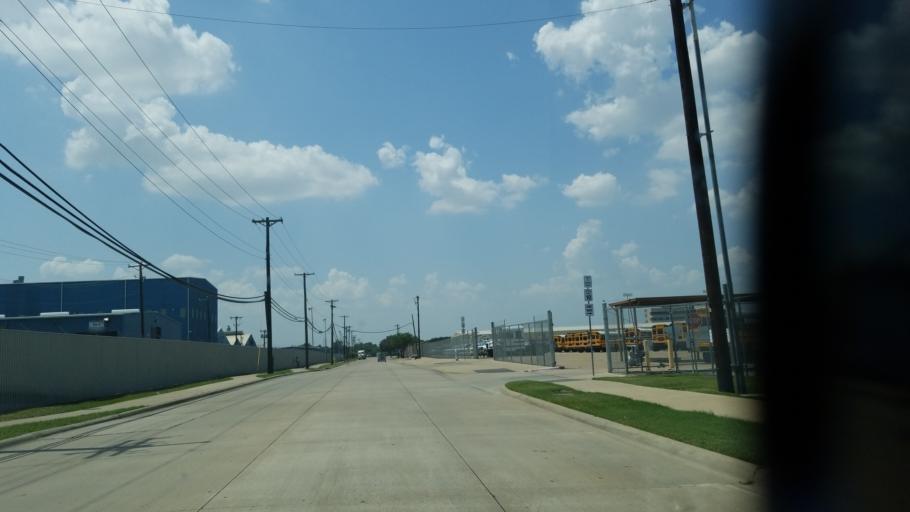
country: US
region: Texas
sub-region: Dallas County
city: Garland
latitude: 32.9238
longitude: -96.6321
